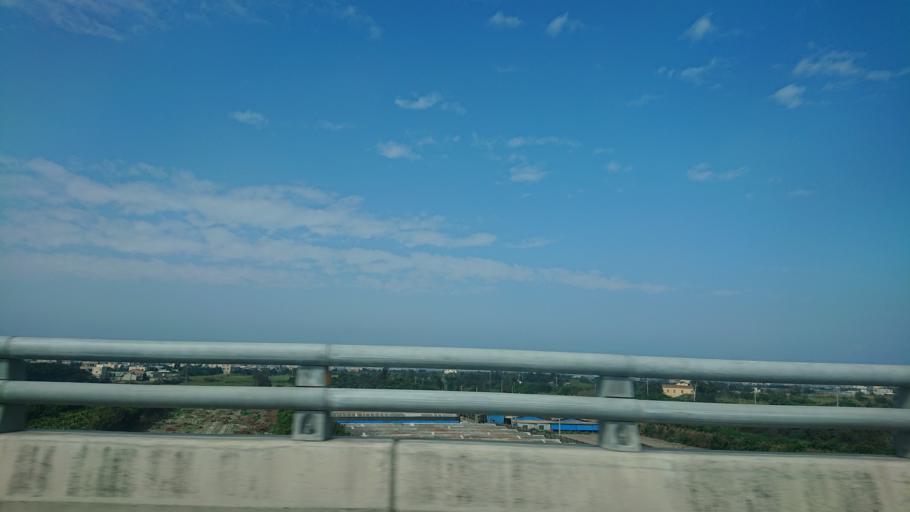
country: TW
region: Taiwan
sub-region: Changhua
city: Chang-hua
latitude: 23.9745
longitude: 120.3605
